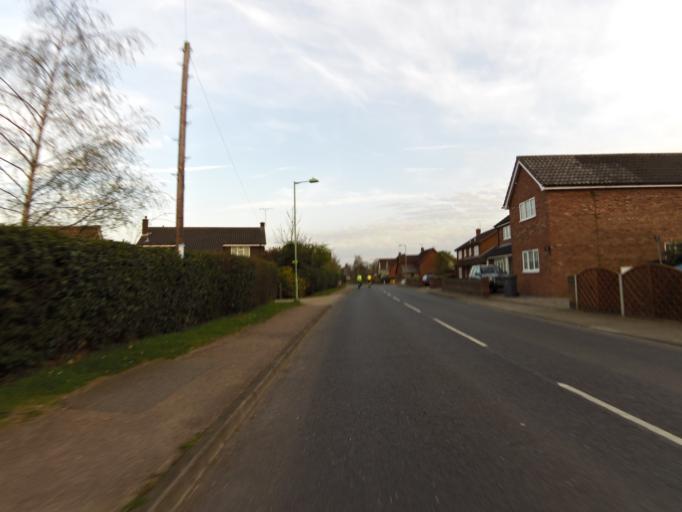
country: GB
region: England
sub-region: Suffolk
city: Debenham
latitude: 52.1519
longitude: 1.2197
